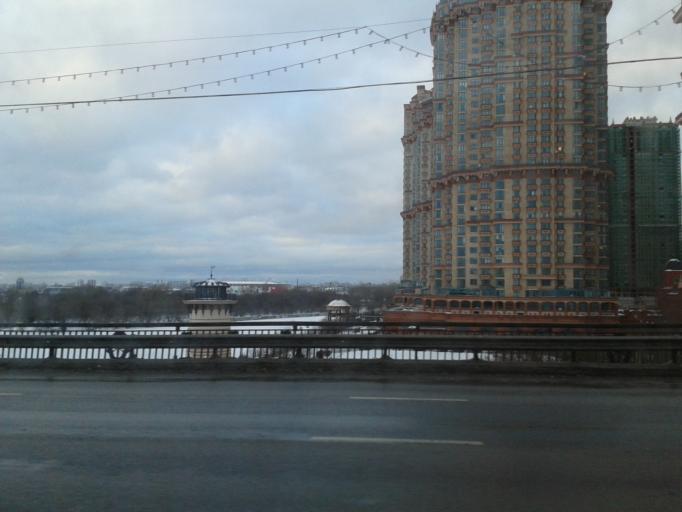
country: RU
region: Moscow
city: Shchukino
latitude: 55.8053
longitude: 37.4488
